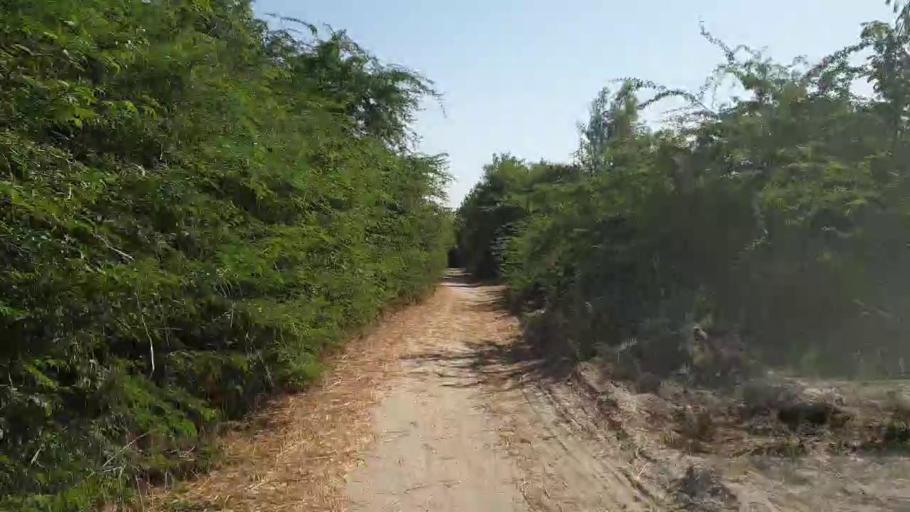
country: PK
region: Sindh
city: Tando Bago
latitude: 24.6494
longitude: 68.9844
